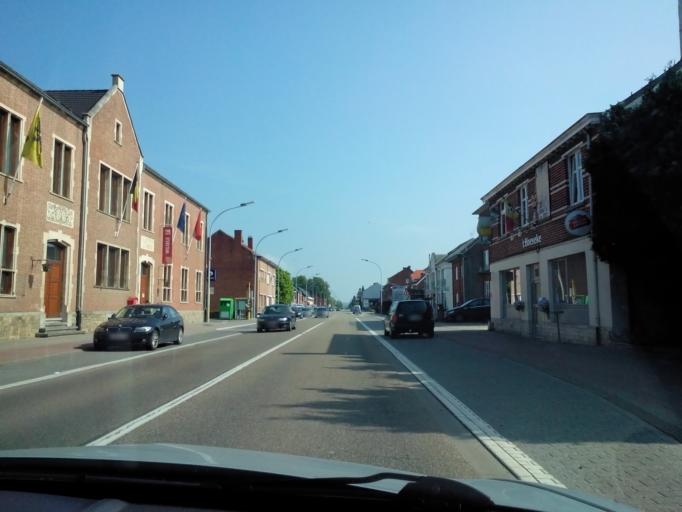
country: BE
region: Flanders
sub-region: Provincie Vlaams-Brabant
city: Leuven
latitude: 50.9104
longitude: 4.7135
